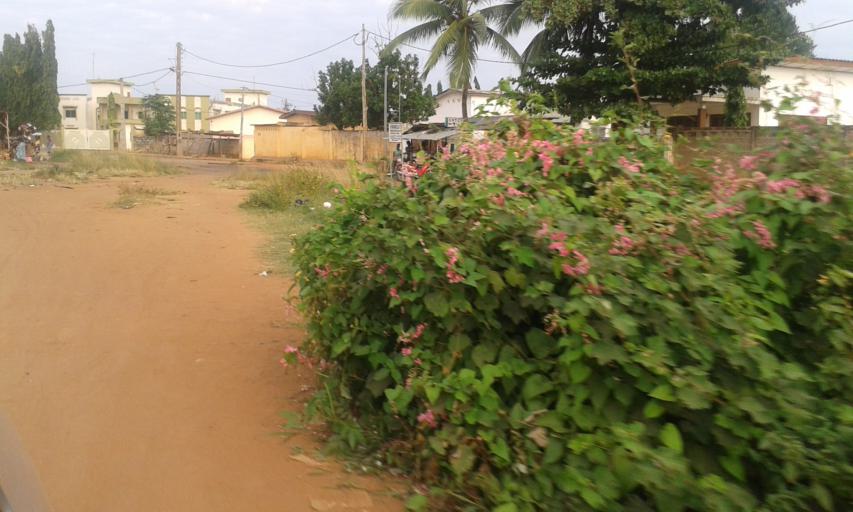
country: BJ
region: Queme
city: Porto-Novo
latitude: 6.4786
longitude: 2.6123
